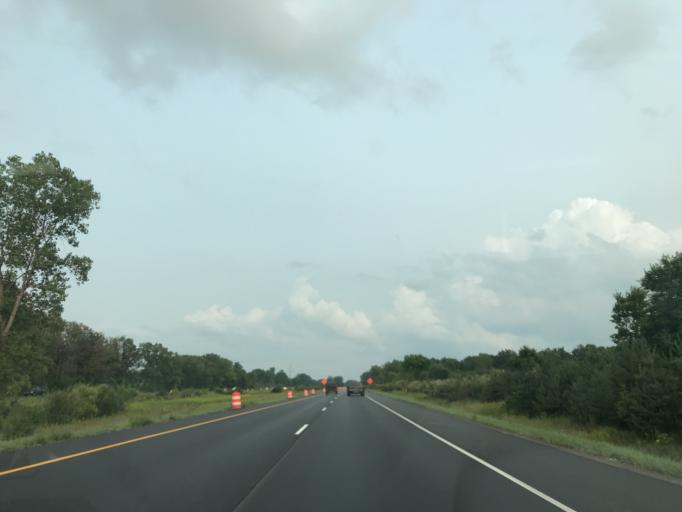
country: US
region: Michigan
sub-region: Livingston County
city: Fowlerville
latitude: 42.6454
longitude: -84.0505
